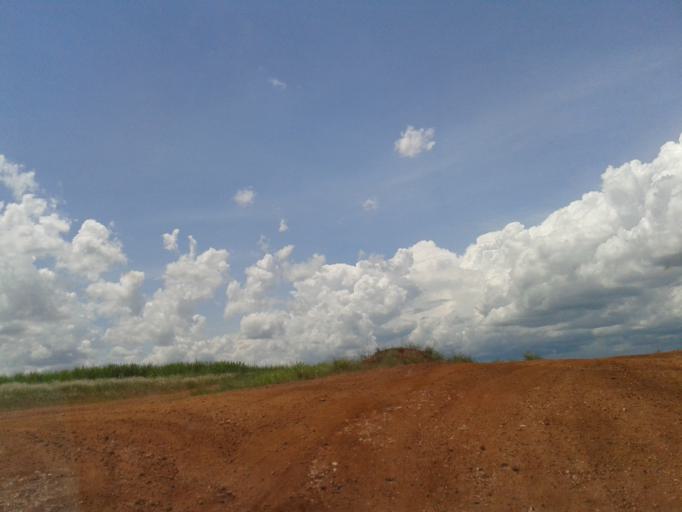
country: BR
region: Minas Gerais
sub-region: Santa Vitoria
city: Santa Vitoria
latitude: -19.1456
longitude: -50.6264
